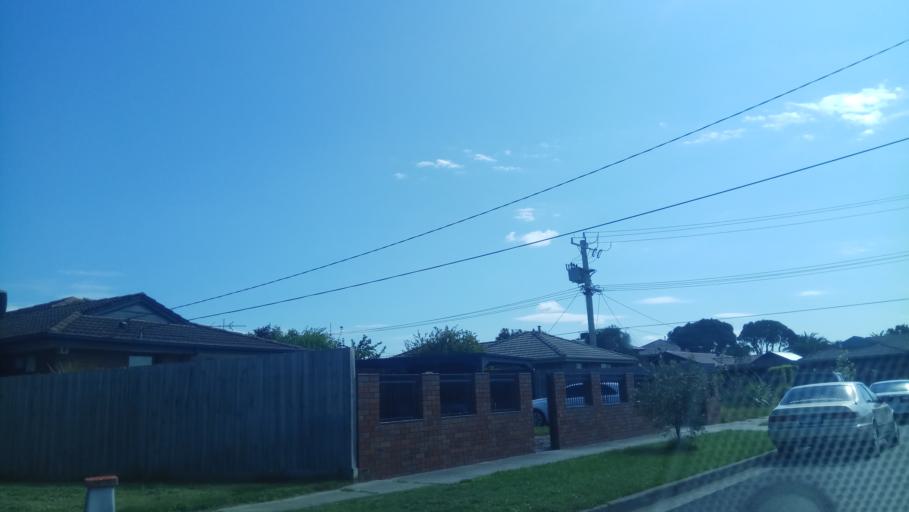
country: AU
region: Victoria
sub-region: Kingston
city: Clayton South
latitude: -37.9442
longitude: 145.0990
